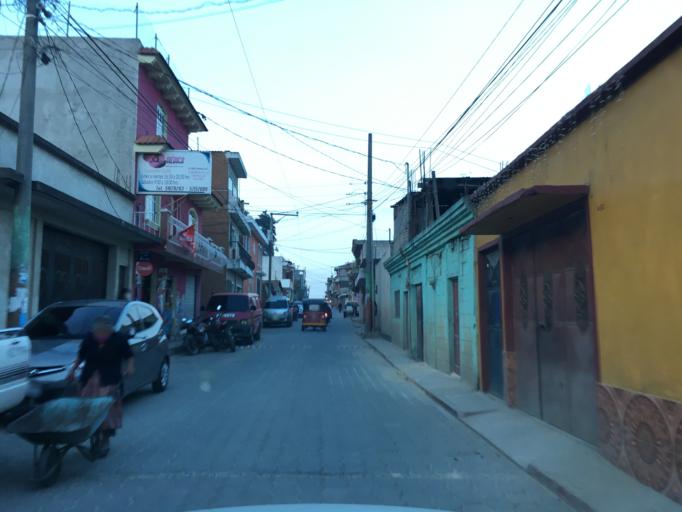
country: GT
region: Chimaltenango
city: Tecpan Guatemala
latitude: 14.7607
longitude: -90.9968
